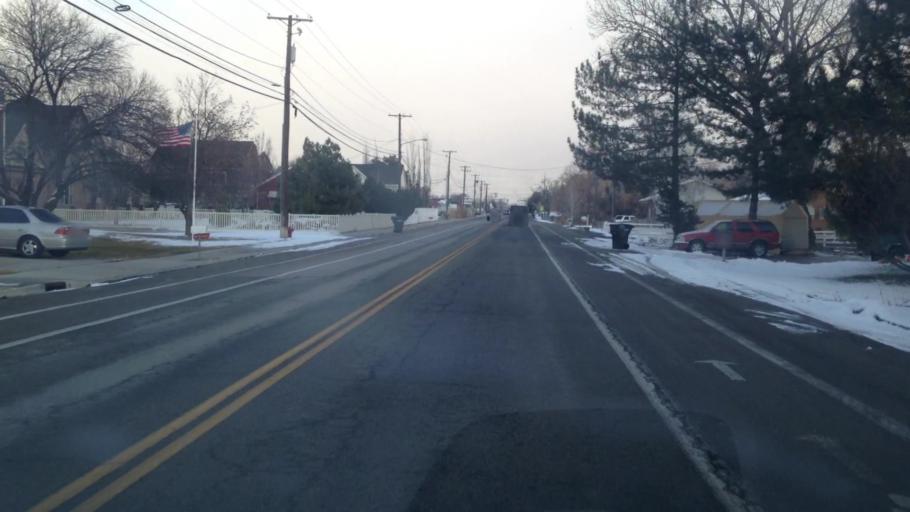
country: US
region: Utah
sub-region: Utah County
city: Provo
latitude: 40.2338
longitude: -111.7001
